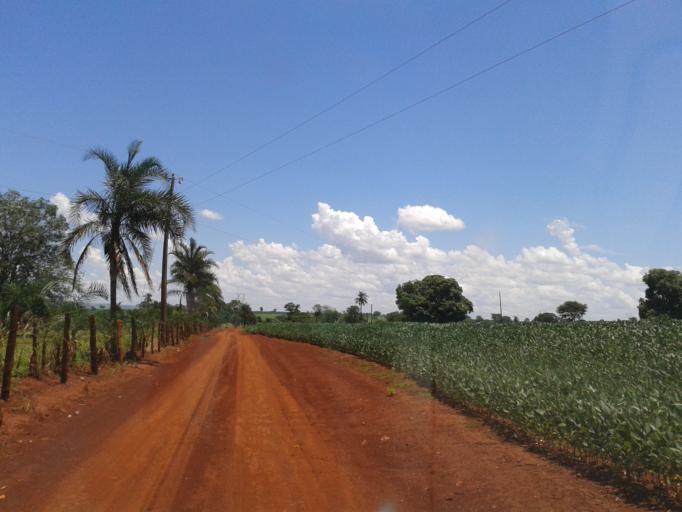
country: BR
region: Minas Gerais
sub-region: Centralina
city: Centralina
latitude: -18.6225
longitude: -49.2961
